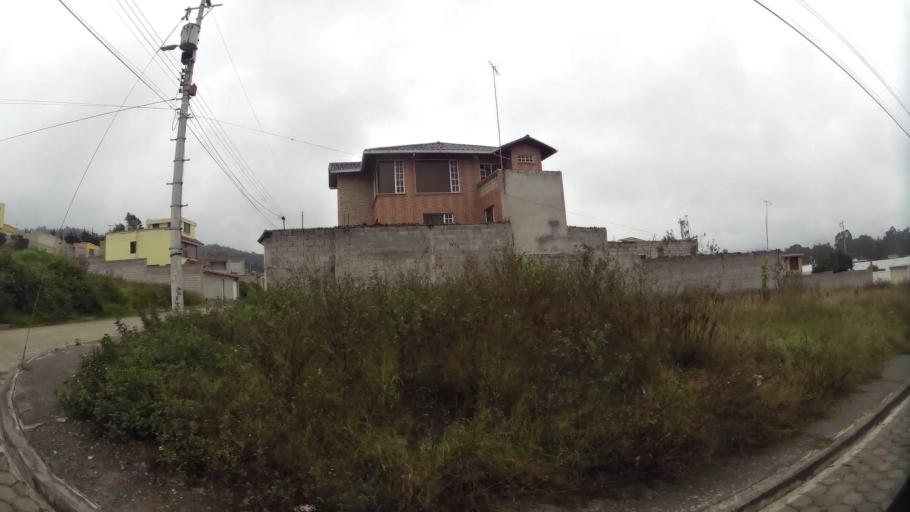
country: EC
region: Pichincha
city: Quito
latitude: -0.2679
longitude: -78.4770
